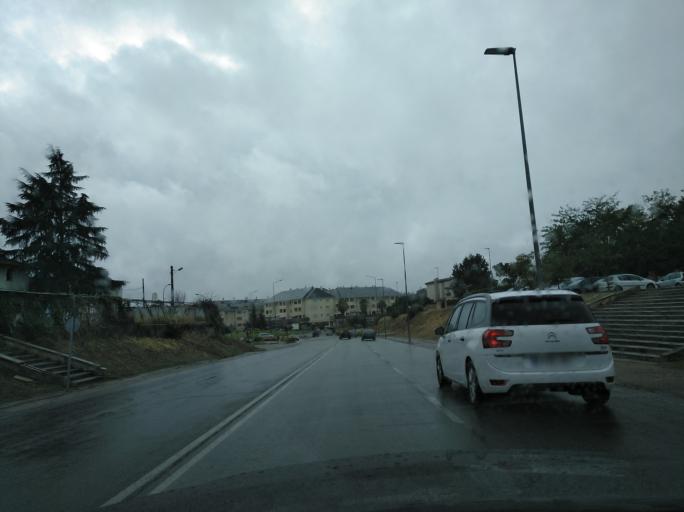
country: ES
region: Extremadura
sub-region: Provincia de Badajoz
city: Badajoz
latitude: 38.8849
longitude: -6.9905
